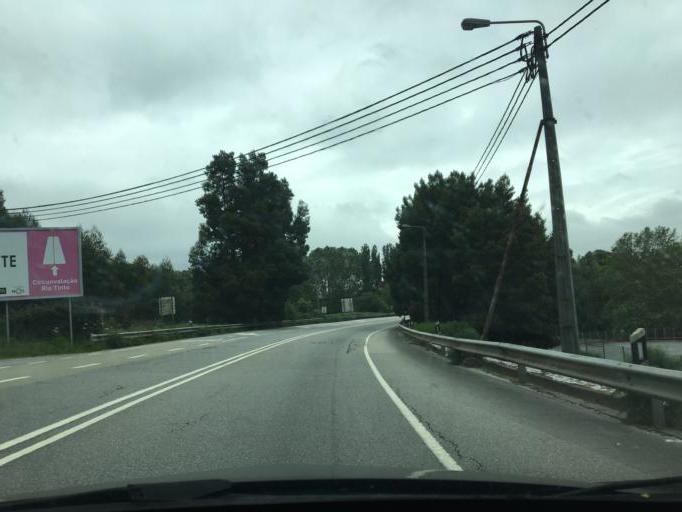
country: PT
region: Porto
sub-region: Maia
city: Maia
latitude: 41.2307
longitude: -8.6357
